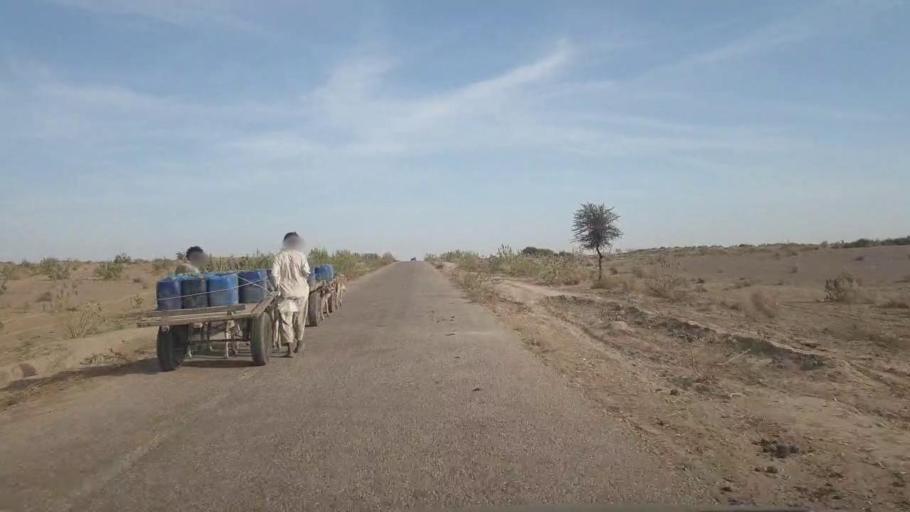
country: PK
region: Sindh
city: Nabisar
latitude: 25.0657
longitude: 69.6515
